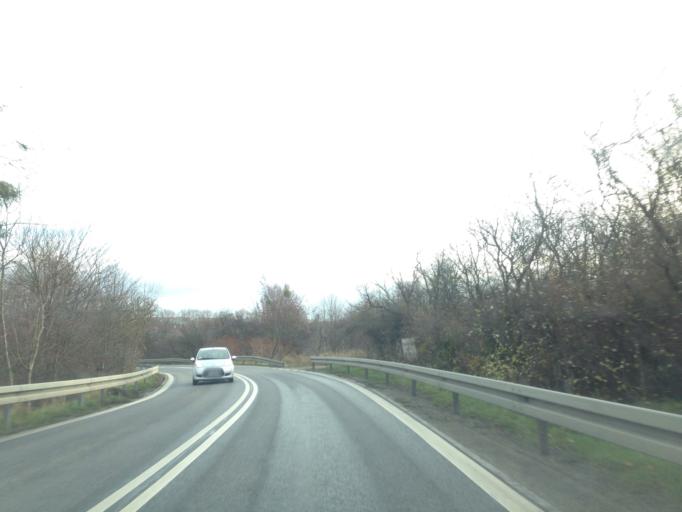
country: PL
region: Pomeranian Voivodeship
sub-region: Powiat gdanski
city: Kowale
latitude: 54.3151
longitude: 18.5777
